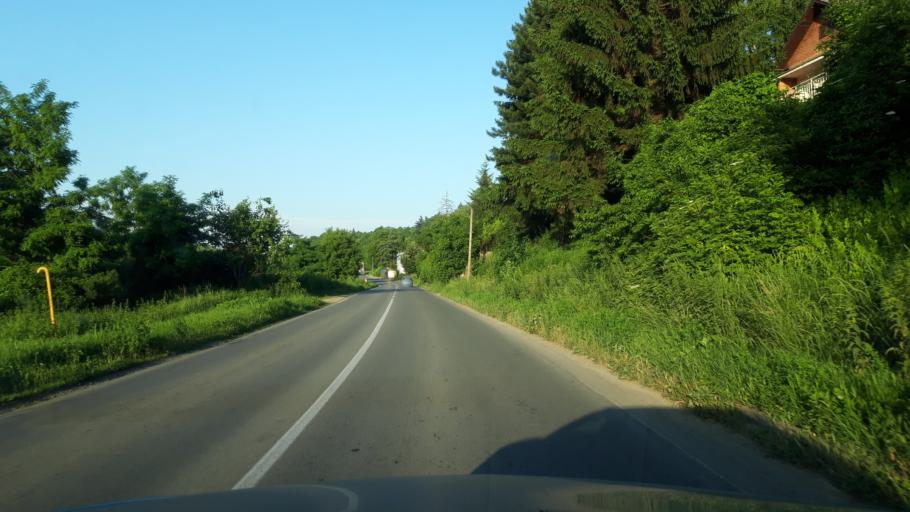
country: RS
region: Autonomna Pokrajina Vojvodina
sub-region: Juznobacki Okrug
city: Beocin
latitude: 45.2087
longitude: 19.7567
